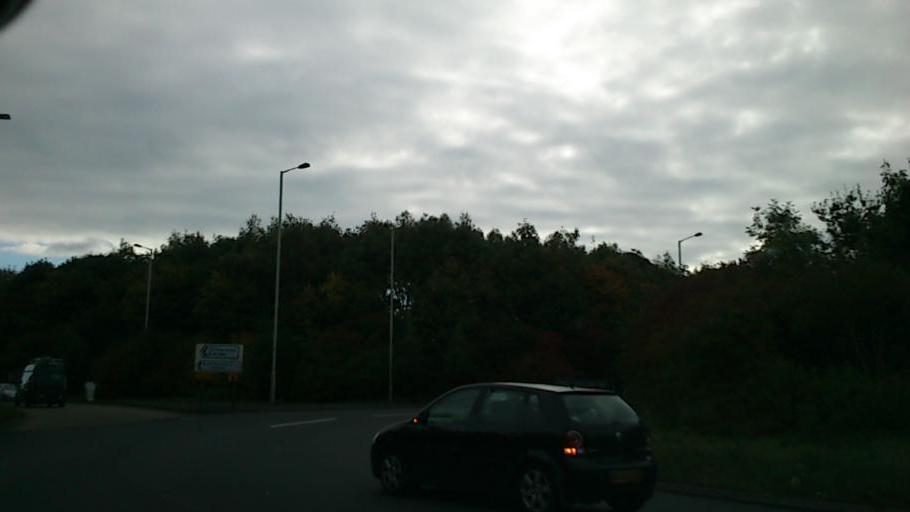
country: GB
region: England
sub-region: Shropshire
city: Great Hanwood
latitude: 52.7031
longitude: -2.8102
